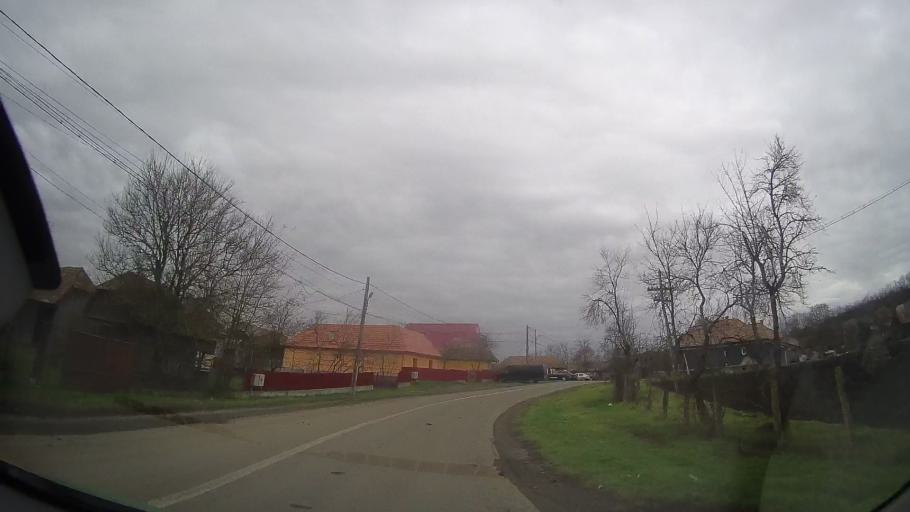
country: RO
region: Mures
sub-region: Comuna Craesti
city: Craiesti
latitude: 46.7580
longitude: 24.4256
